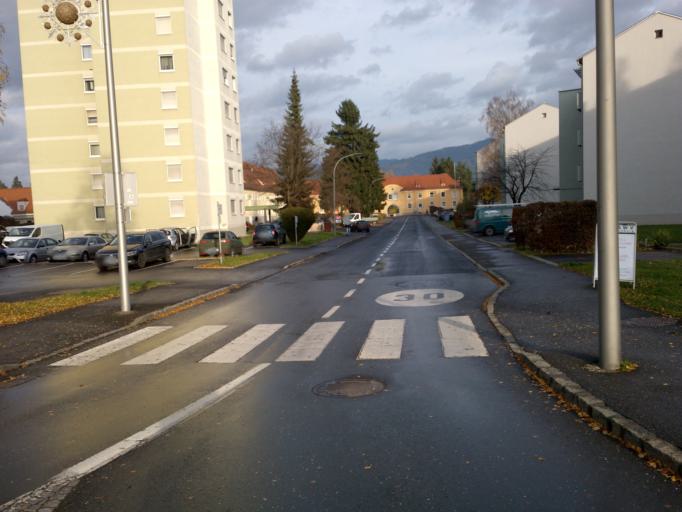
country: AT
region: Styria
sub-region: Politischer Bezirk Murtal
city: Judenburg
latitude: 47.1762
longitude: 14.6763
